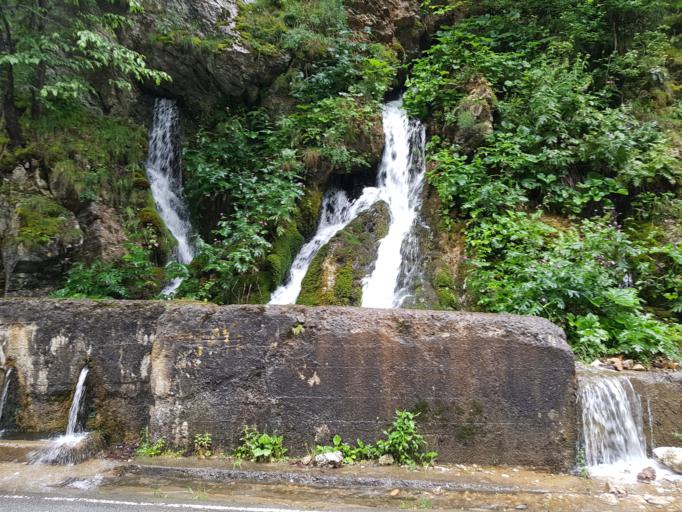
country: ME
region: Mojkovac
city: Mojkovac
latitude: 43.0731
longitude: 19.3846
